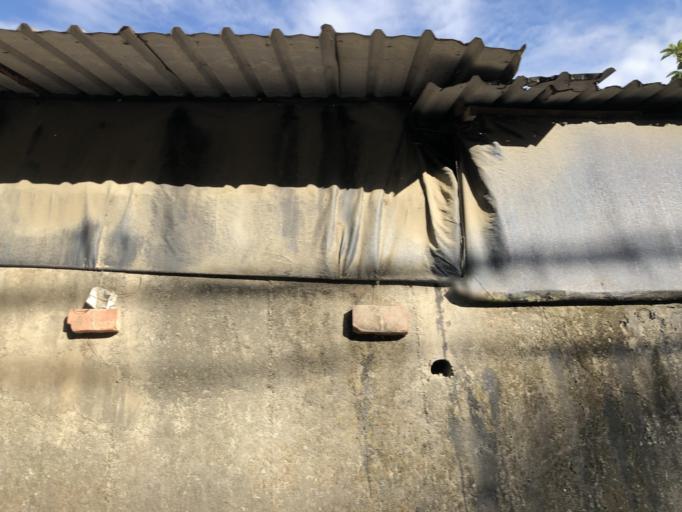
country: TW
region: Taiwan
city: Yujing
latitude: 23.0175
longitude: 120.3974
